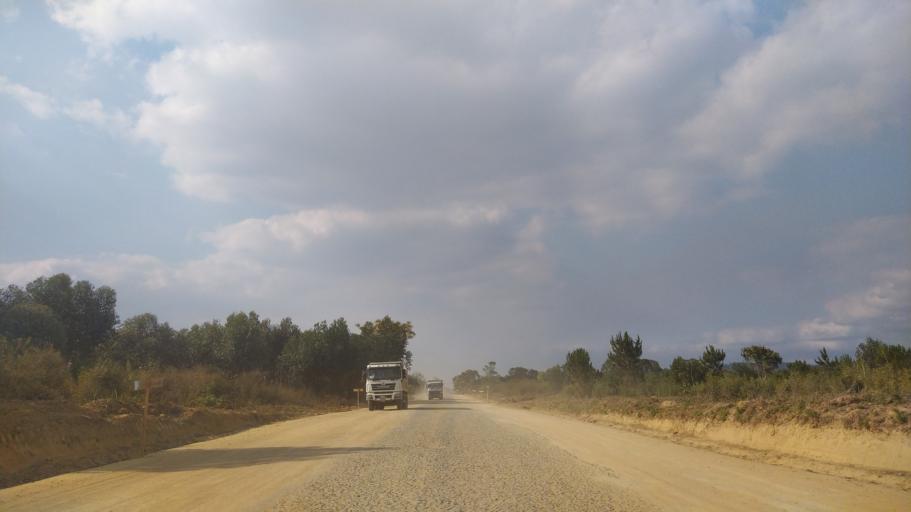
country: MG
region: Alaotra Mangoro
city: Moramanga
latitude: -18.6392
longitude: 48.2757
